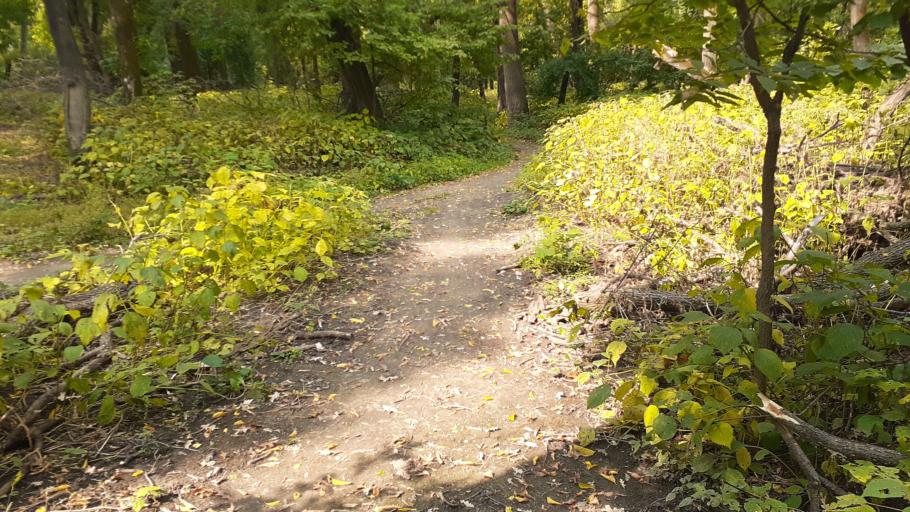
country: US
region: Minnesota
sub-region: Clay County
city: Oakport
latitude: 46.9107
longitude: -96.7597
